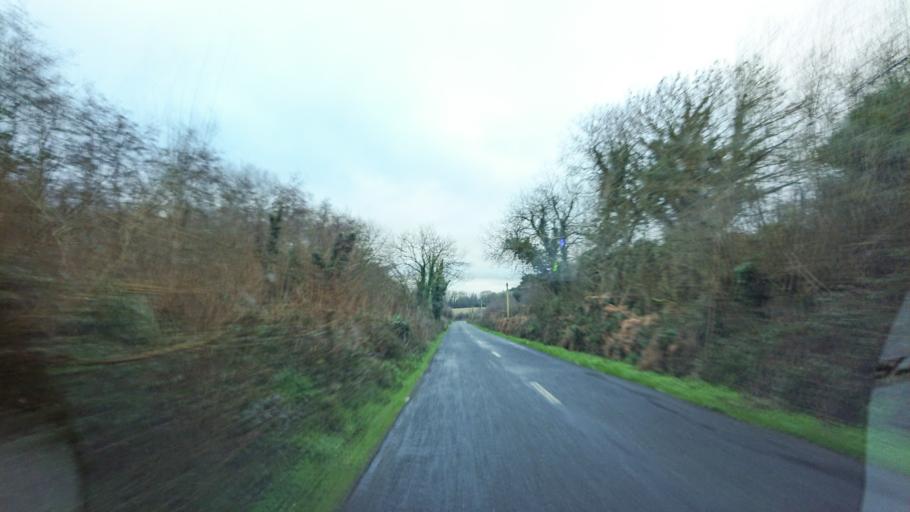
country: IE
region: Munster
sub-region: Waterford
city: Portlaw
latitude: 52.2175
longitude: -7.4166
